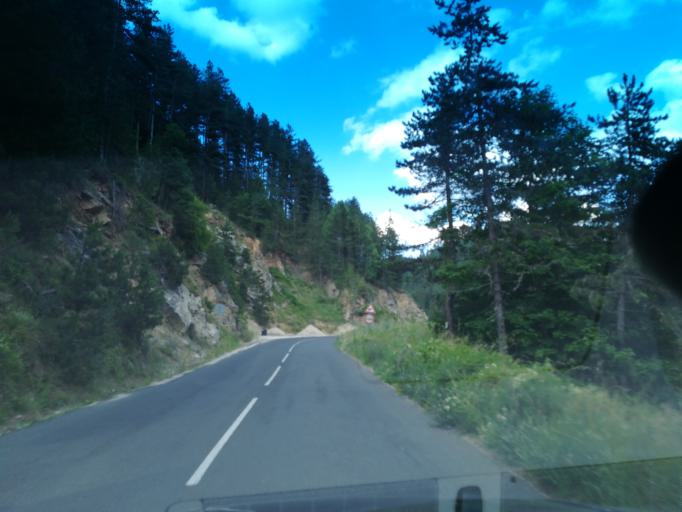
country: BG
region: Smolyan
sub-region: Obshtina Smolyan
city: Smolyan
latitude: 41.6479
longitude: 24.7667
